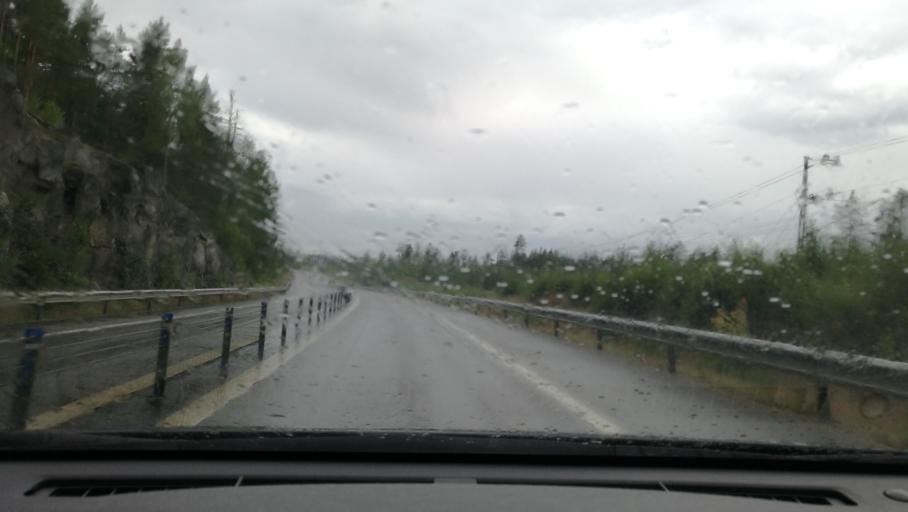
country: SE
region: OEstergoetland
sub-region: Norrkopings Kommun
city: Jursla
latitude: 58.8133
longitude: 16.1544
